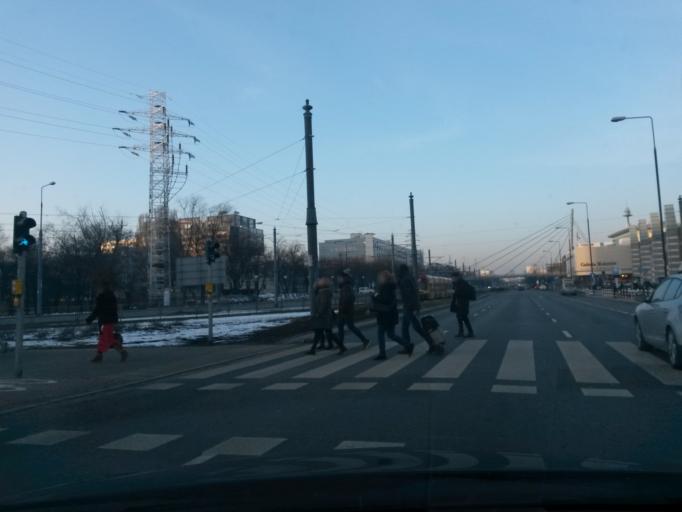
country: PL
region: Masovian Voivodeship
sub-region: Warszawa
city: Mokotow
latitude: 52.1785
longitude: 21.0025
